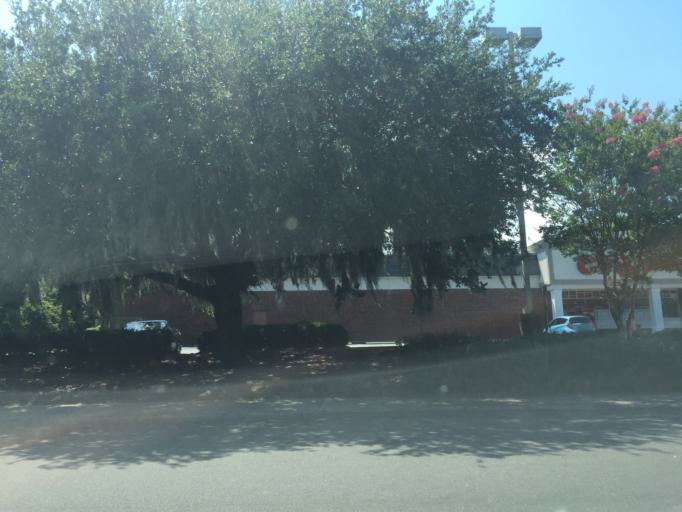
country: US
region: Georgia
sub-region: Chatham County
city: Montgomery
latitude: 31.9820
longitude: -81.1531
